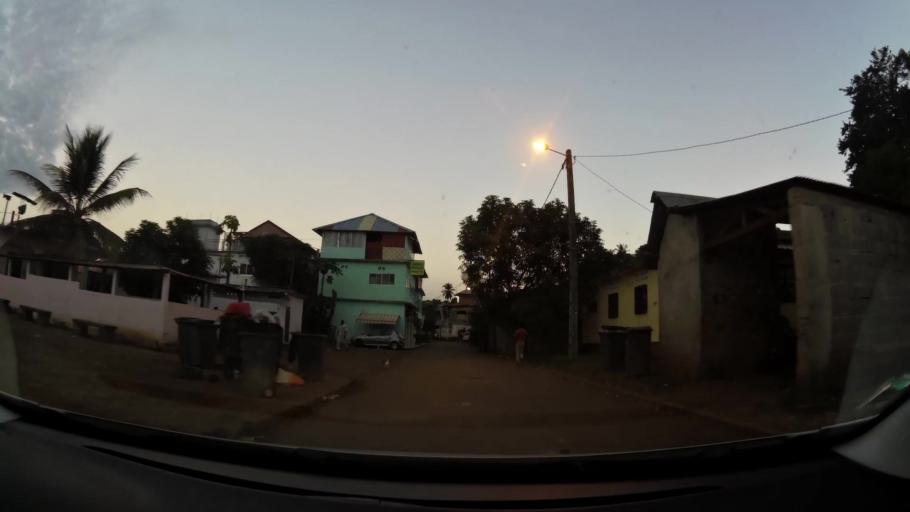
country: YT
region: Bandraboua
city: Bandraboua
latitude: -12.7341
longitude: 45.1385
